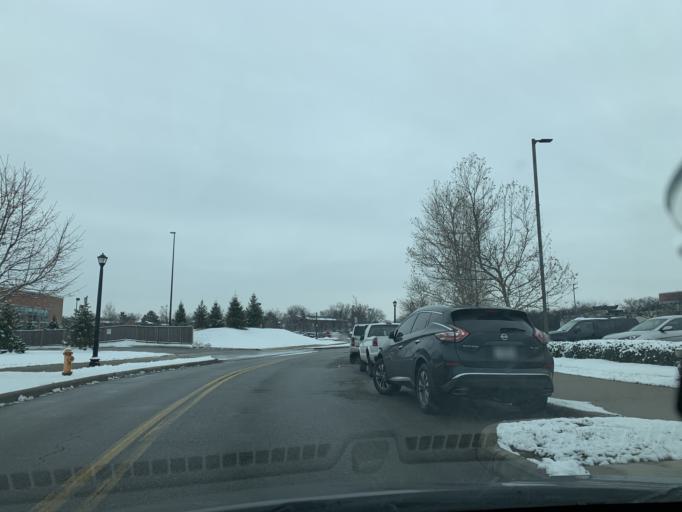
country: US
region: Ohio
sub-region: Franklin County
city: Minerva Park
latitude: 40.0585
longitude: -82.9740
